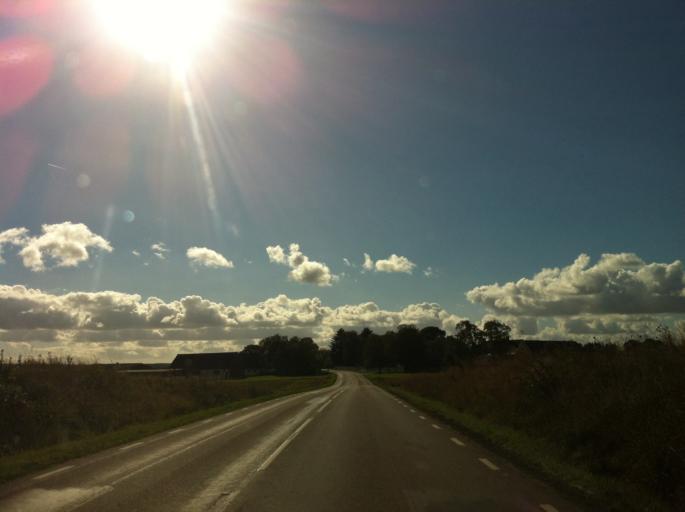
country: SE
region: Skane
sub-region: Sjobo Kommun
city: Sjoebo
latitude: 55.6519
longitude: 13.8118
